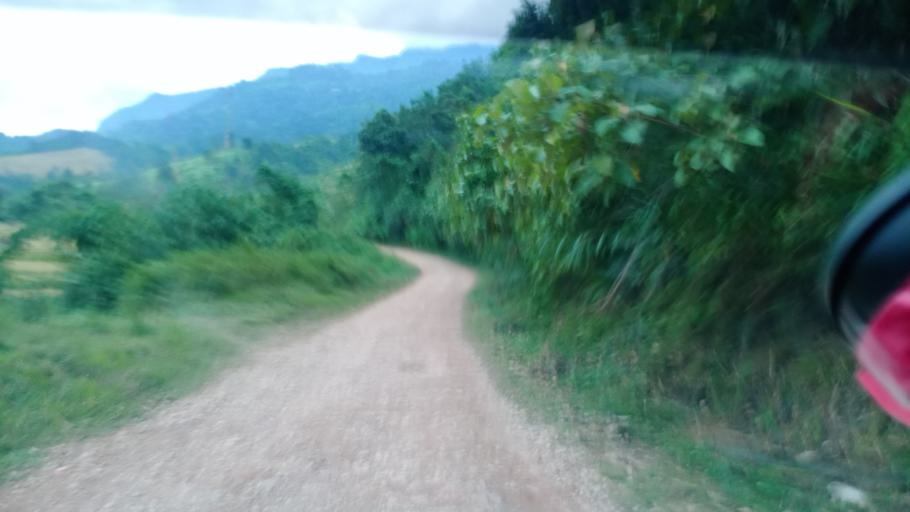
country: TH
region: Changwat Bueng Kan
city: Pak Khat
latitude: 18.7146
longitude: 103.2148
